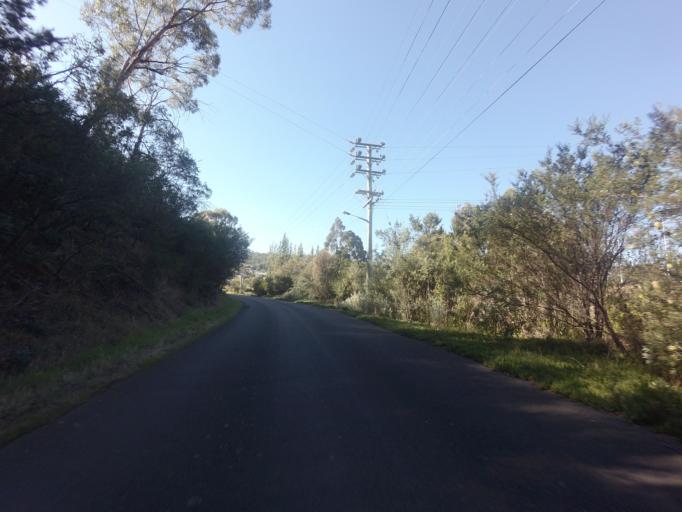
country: AU
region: Tasmania
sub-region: Clarence
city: Lindisfarne
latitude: -42.8358
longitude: 147.3464
